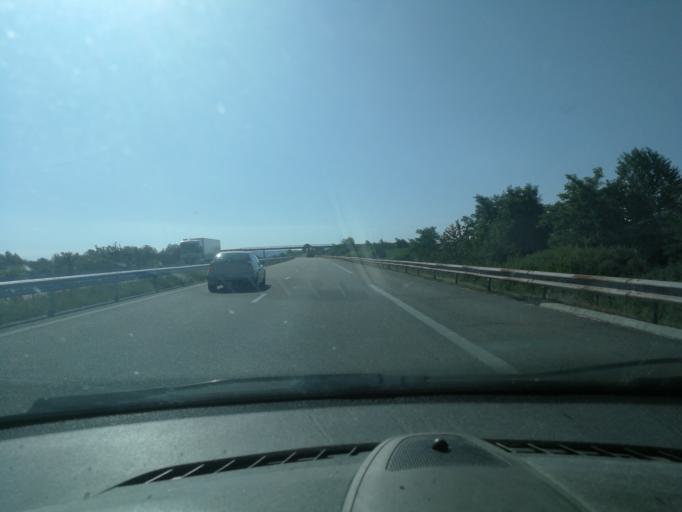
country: FR
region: Alsace
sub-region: Departement du Bas-Rhin
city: Drulingen
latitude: 48.8022
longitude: 7.1828
